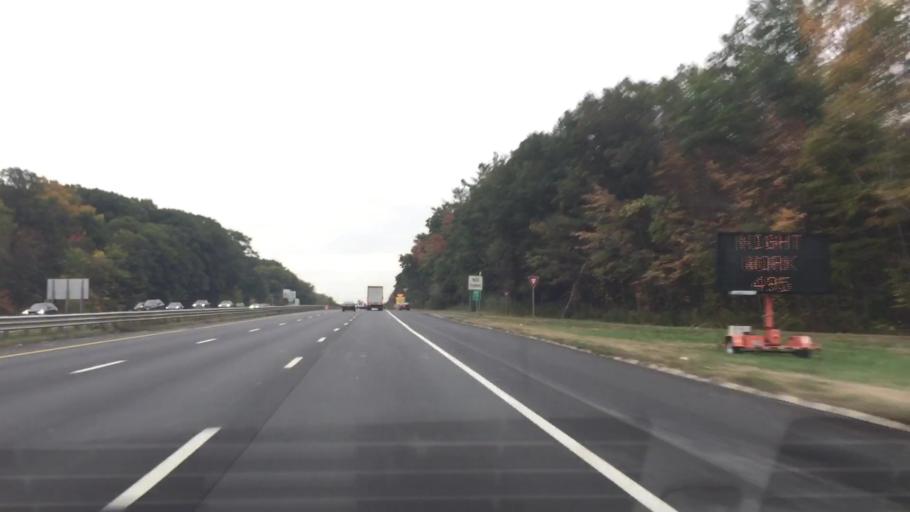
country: US
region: Massachusetts
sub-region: Essex County
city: Methuen
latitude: 42.6915
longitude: -71.2070
